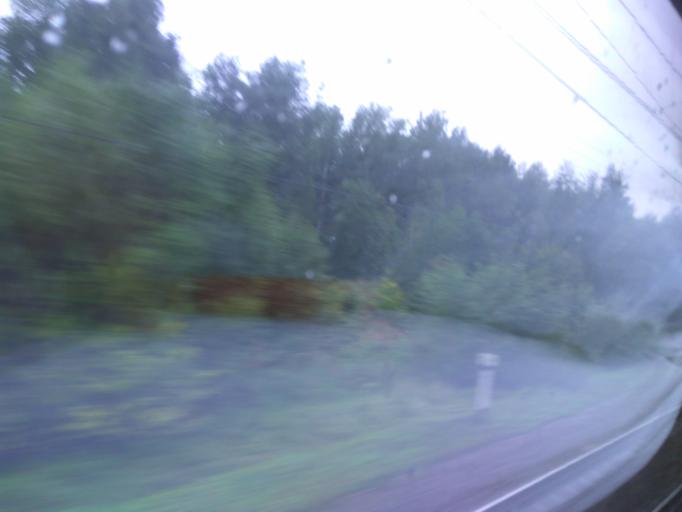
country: RU
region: Moskovskaya
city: Ozery
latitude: 54.7129
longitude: 38.4552
